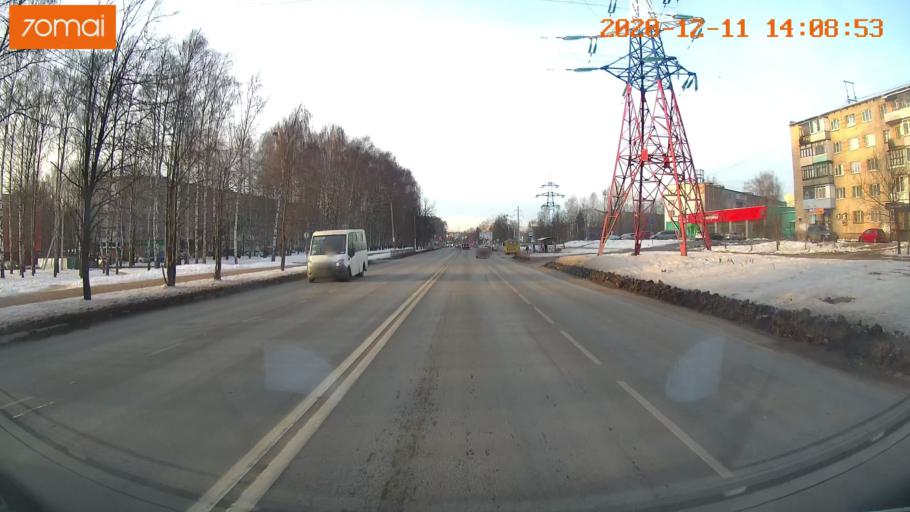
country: RU
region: Kostroma
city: Oktyabr'skiy
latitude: 57.7377
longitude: 40.9915
